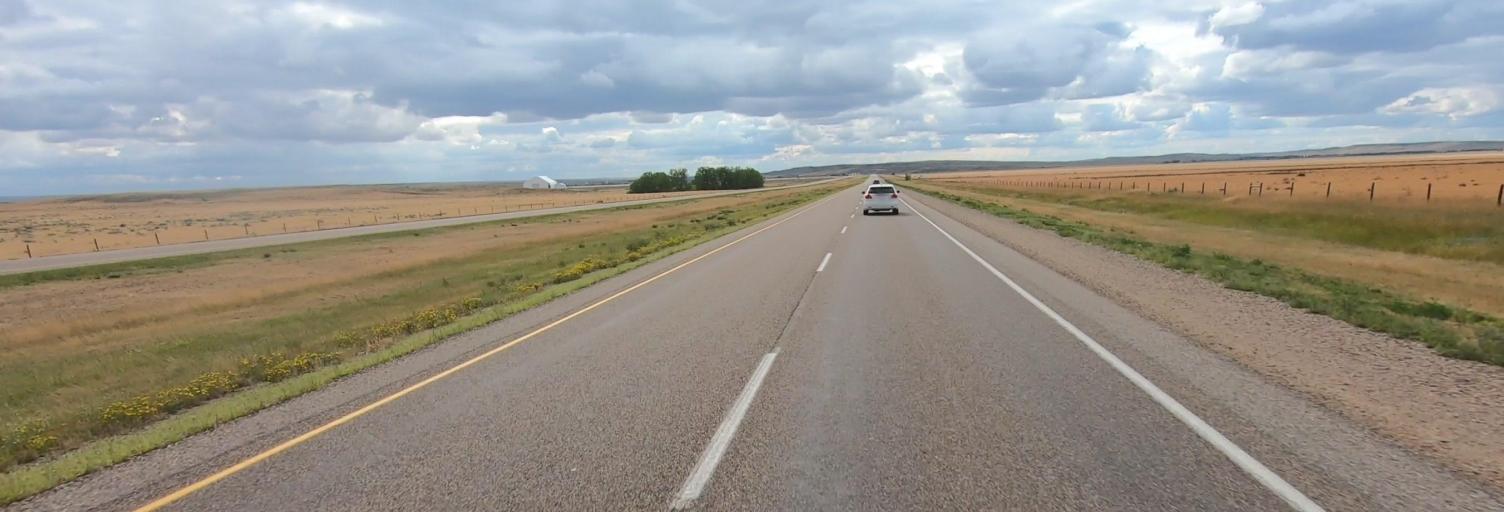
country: CA
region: Saskatchewan
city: Maple Creek
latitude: 49.9608
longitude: -109.9544
